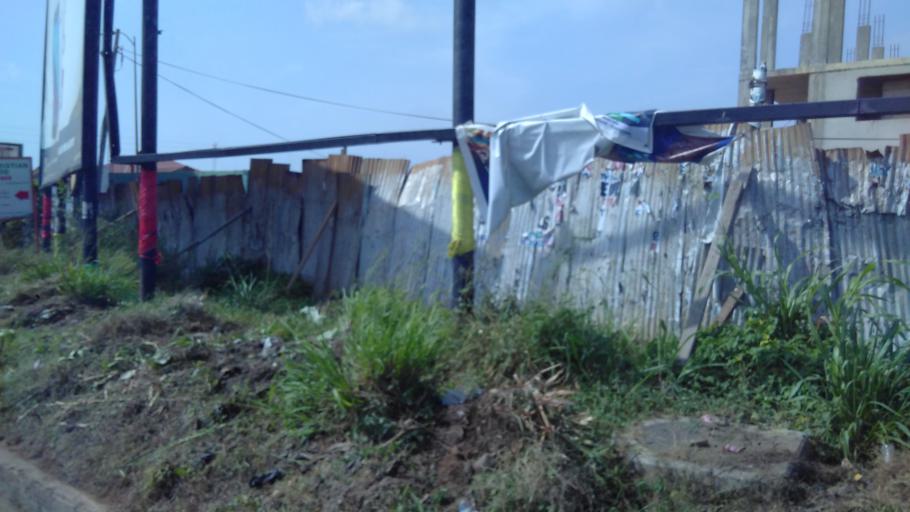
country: GH
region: Greater Accra
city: Nungua
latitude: 5.6146
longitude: -0.0731
